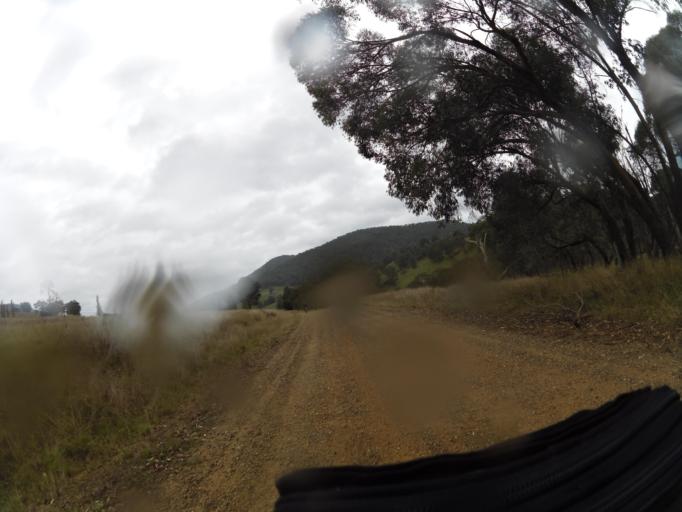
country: AU
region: New South Wales
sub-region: Greater Hume Shire
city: Holbrook
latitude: -36.2390
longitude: 147.6340
